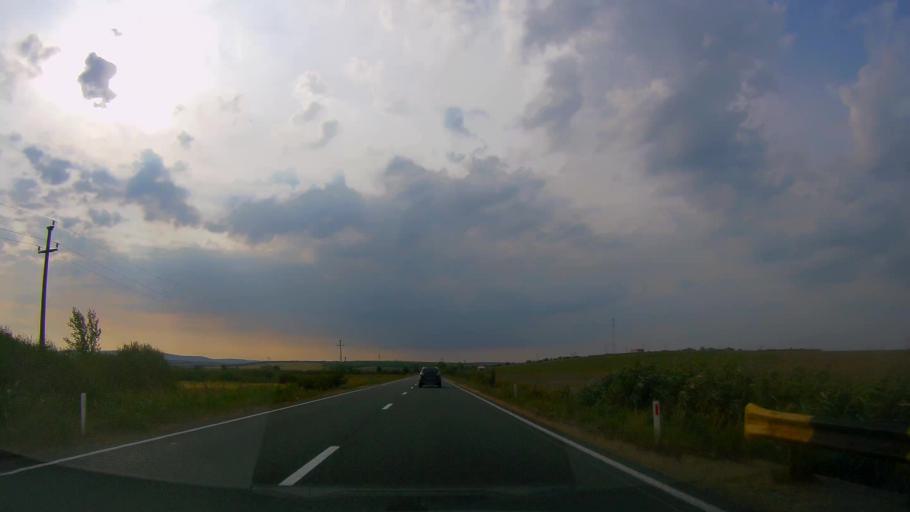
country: RO
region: Satu Mare
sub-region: Oras Ardud
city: Ardud
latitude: 47.6171
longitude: 22.8749
